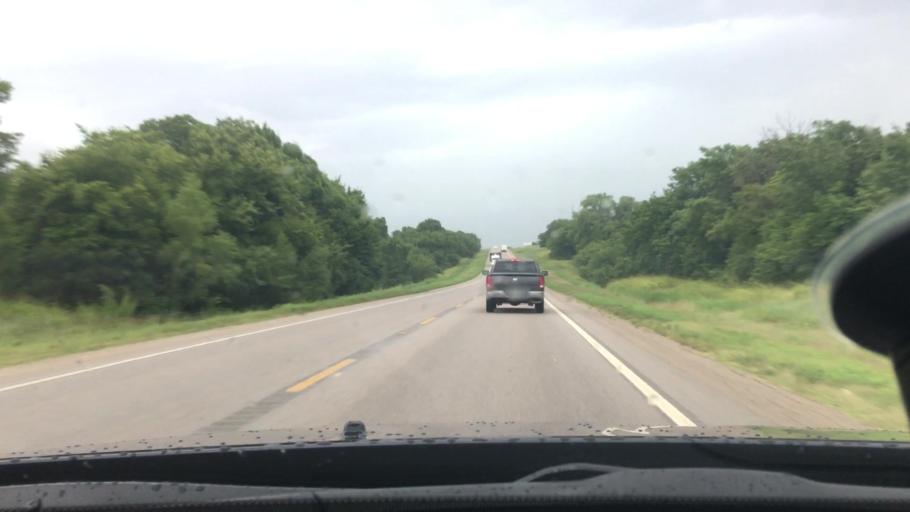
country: US
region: Oklahoma
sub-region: Marshall County
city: Oakland
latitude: 34.1001
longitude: -96.8270
